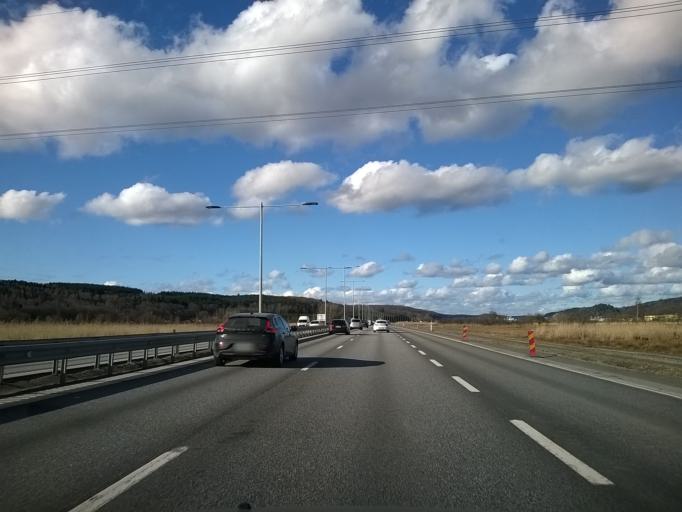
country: SE
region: Vaestra Goetaland
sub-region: Ale Kommun
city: Surte
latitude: 57.8163
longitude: 12.0054
